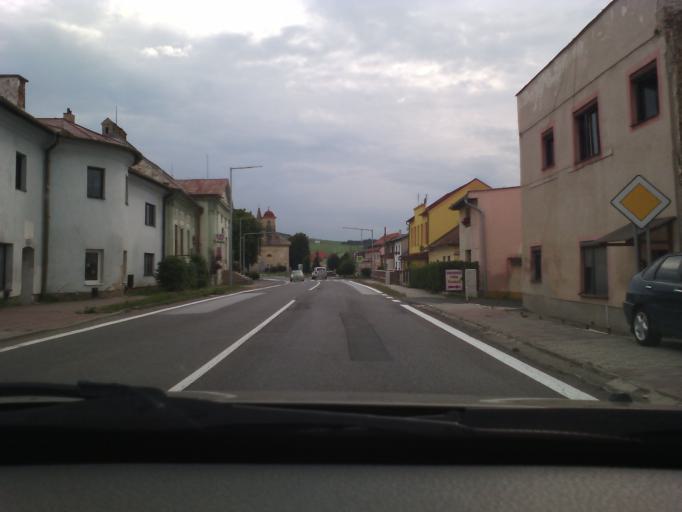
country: SK
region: Presovsky
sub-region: Okres Presov
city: Kezmarok
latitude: 49.1170
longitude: 20.3795
